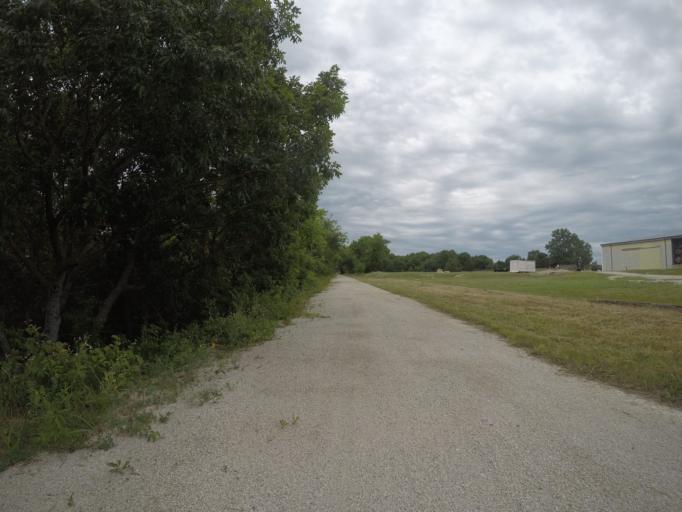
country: US
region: Kansas
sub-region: Anderson County
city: Garnett
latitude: 38.3193
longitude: -95.2498
